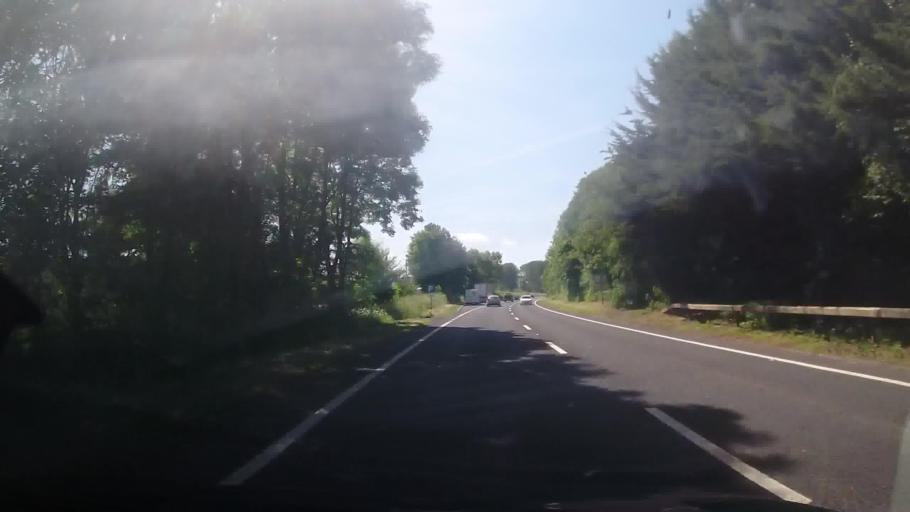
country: GB
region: England
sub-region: Herefordshire
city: Hope under Dinmore
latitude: 52.1878
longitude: -2.7158
